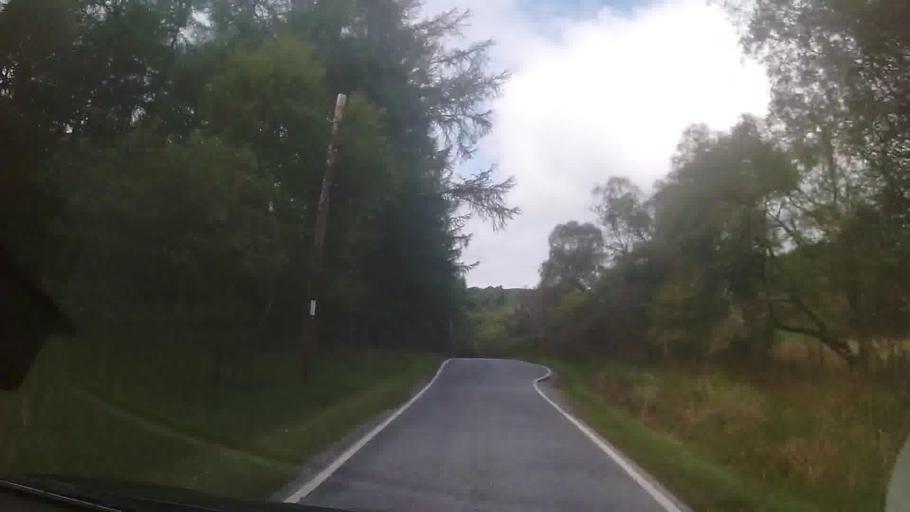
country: GB
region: Scotland
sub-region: Argyll and Bute
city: Isle Of Mull
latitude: 56.7144
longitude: -5.7519
